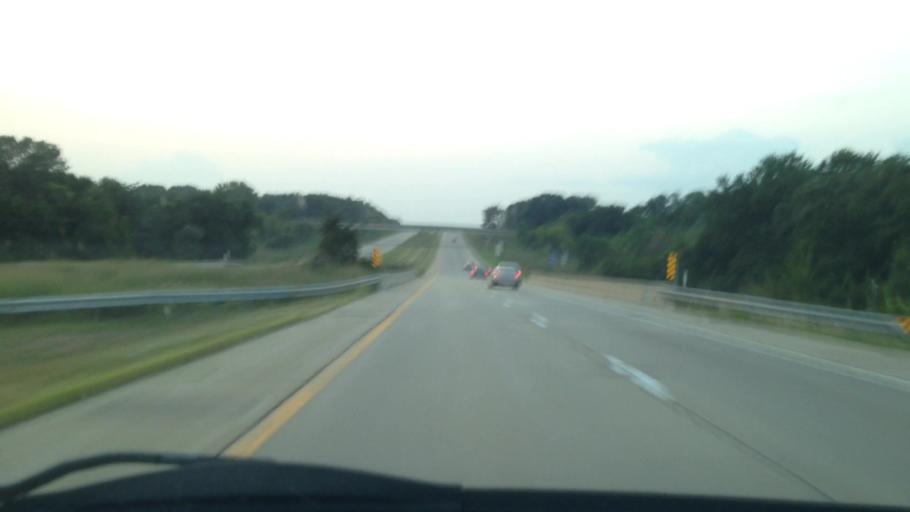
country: US
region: Iowa
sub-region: Benton County
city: Urbana
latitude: 42.3181
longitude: -91.9848
